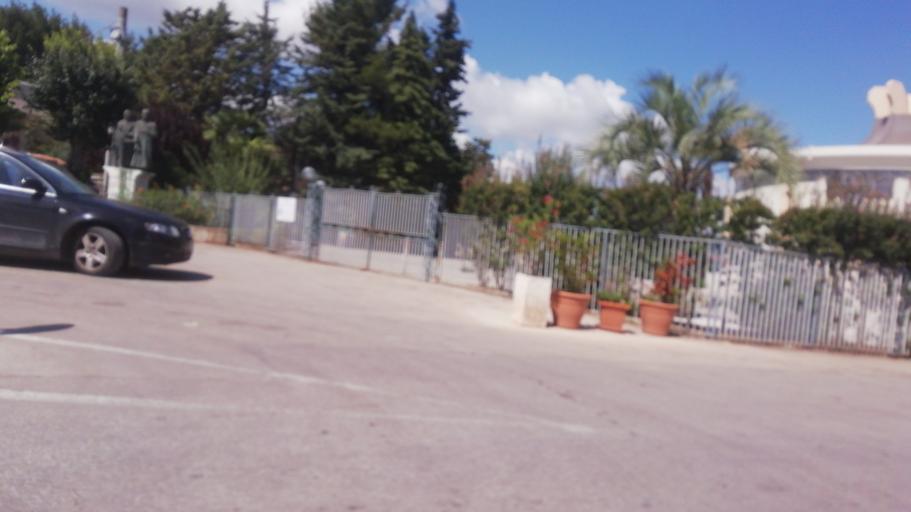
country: IT
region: Apulia
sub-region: Provincia di Bari
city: Corato
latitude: 41.1281
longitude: 16.3824
